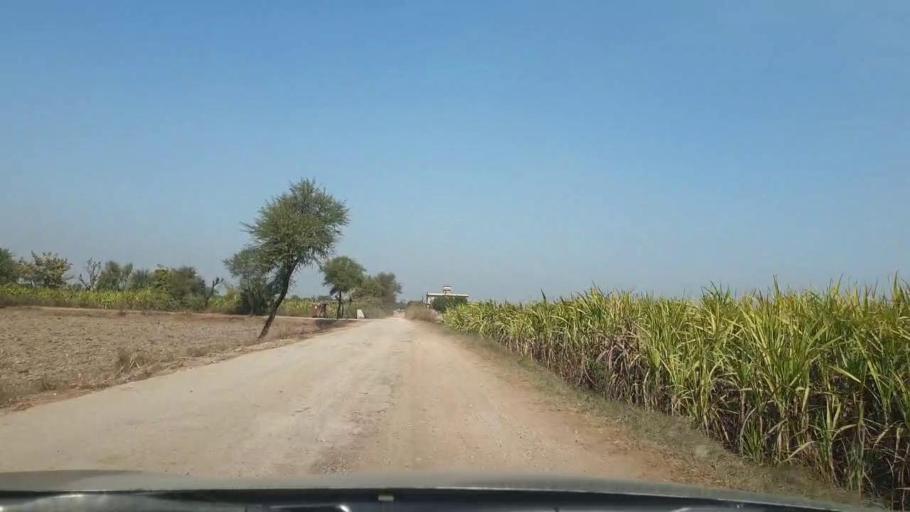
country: PK
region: Sindh
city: Tando Adam
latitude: 25.6147
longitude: 68.6462
